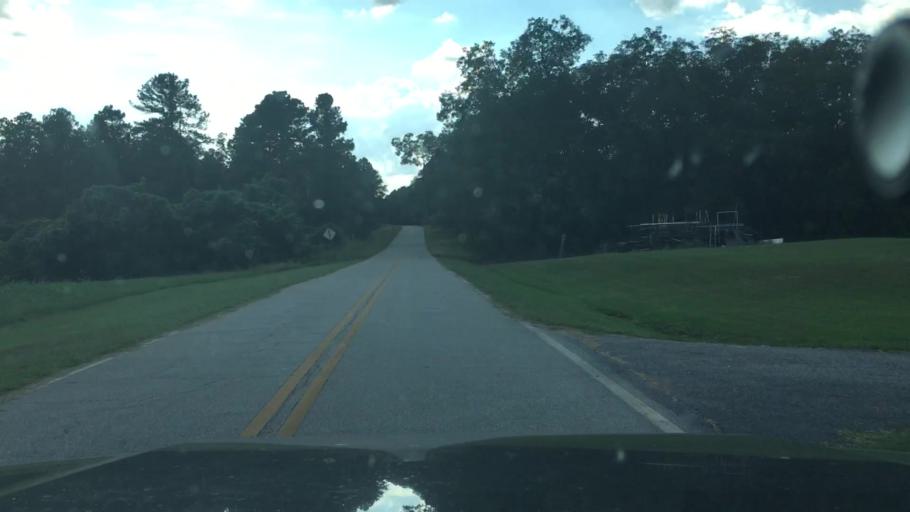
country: US
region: Georgia
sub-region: Monroe County
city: Forsyth
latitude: 32.9988
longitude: -83.8805
